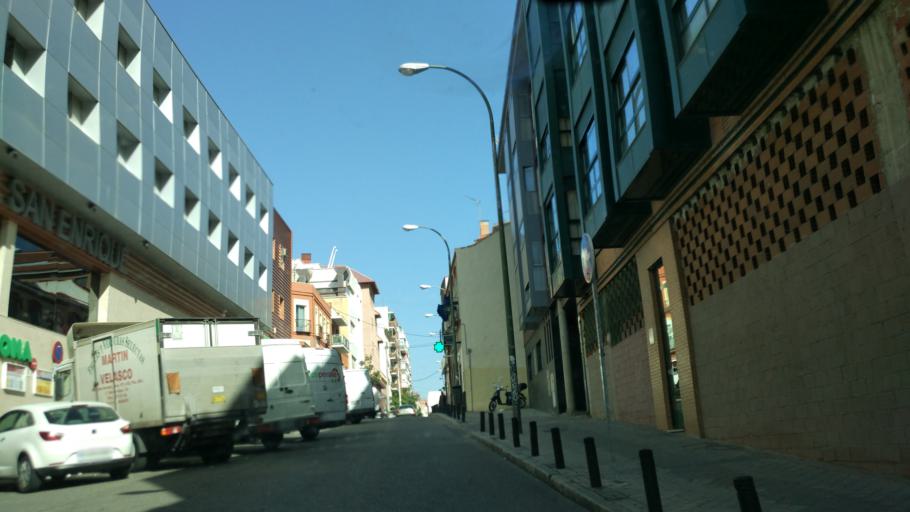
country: ES
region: Madrid
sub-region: Provincia de Madrid
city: Tetuan de las Victorias
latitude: 40.4555
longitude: -3.7003
